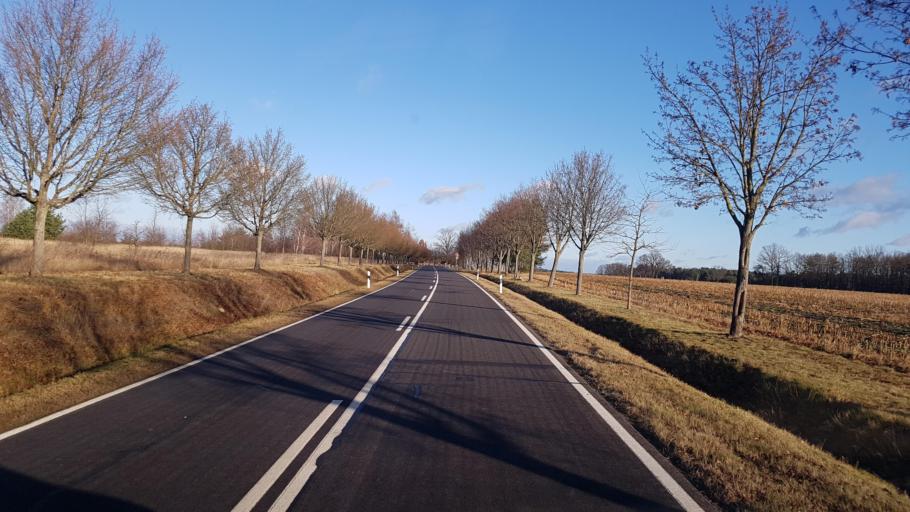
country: DE
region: Brandenburg
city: Forst
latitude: 51.7527
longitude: 14.5624
